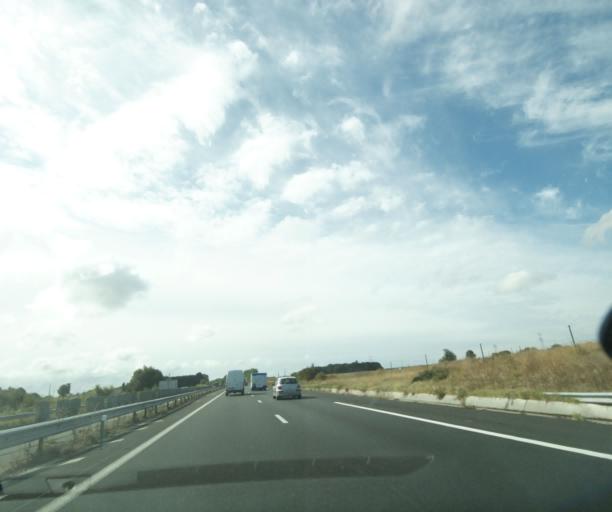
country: FR
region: Poitou-Charentes
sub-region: Departement de la Charente-Maritime
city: Pons
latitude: 45.5877
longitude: -0.5940
